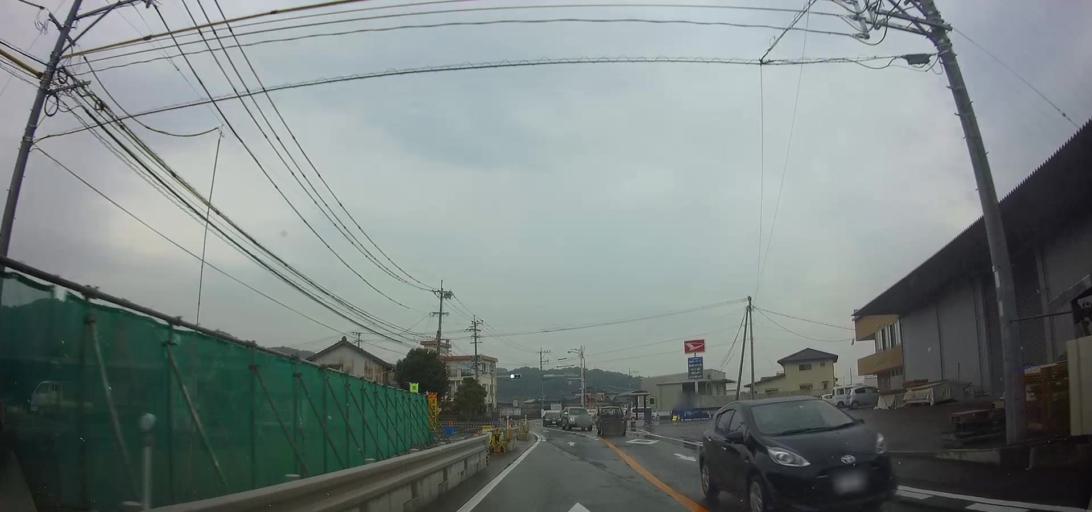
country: JP
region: Nagasaki
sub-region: Isahaya-shi
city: Isahaya
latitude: 32.8345
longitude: 130.1129
